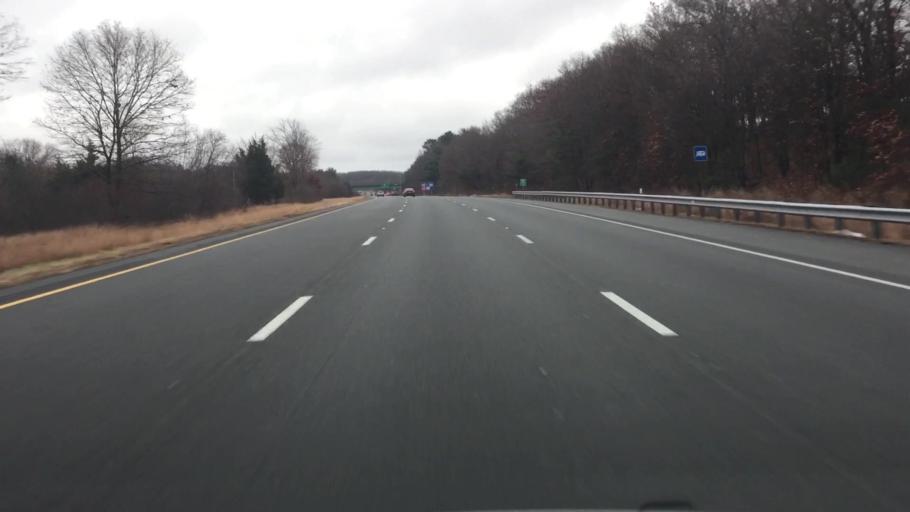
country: US
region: Massachusetts
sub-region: Norfolk County
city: Bellingham
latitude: 42.1191
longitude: -71.4703
